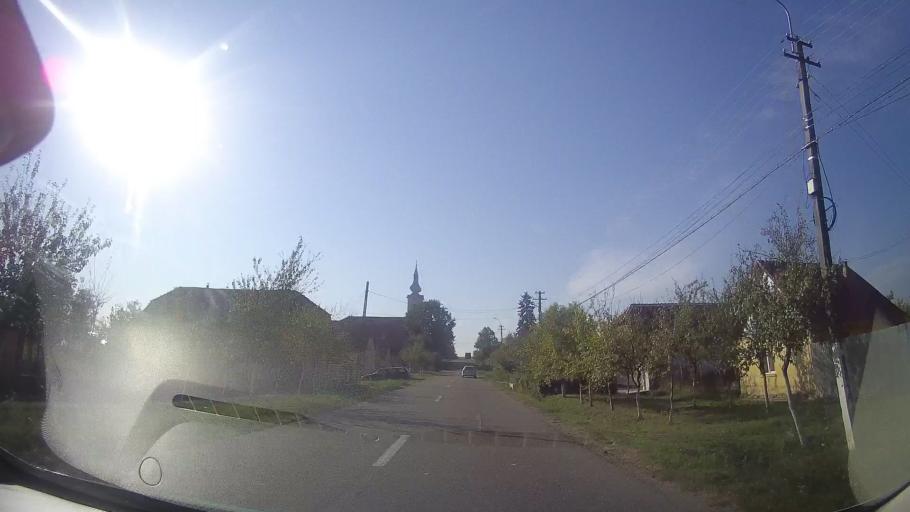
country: RO
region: Timis
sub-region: Oras Recas
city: Recas
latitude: 45.8596
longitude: 21.5153
